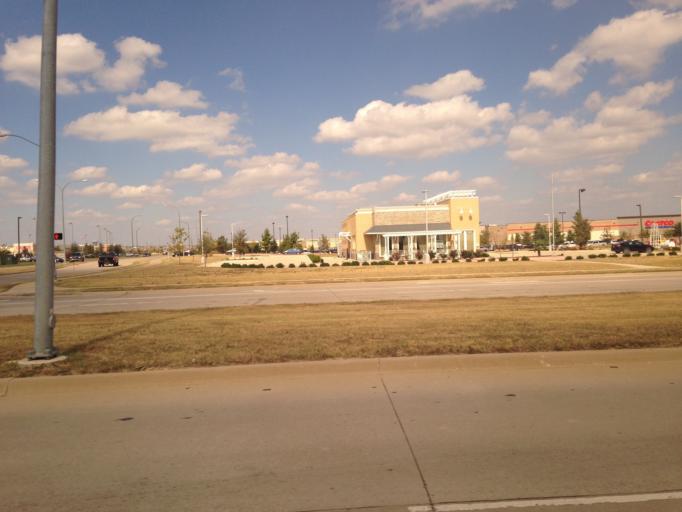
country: US
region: Texas
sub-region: Tarrant County
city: Blue Mound
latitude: 32.8984
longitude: -97.3216
